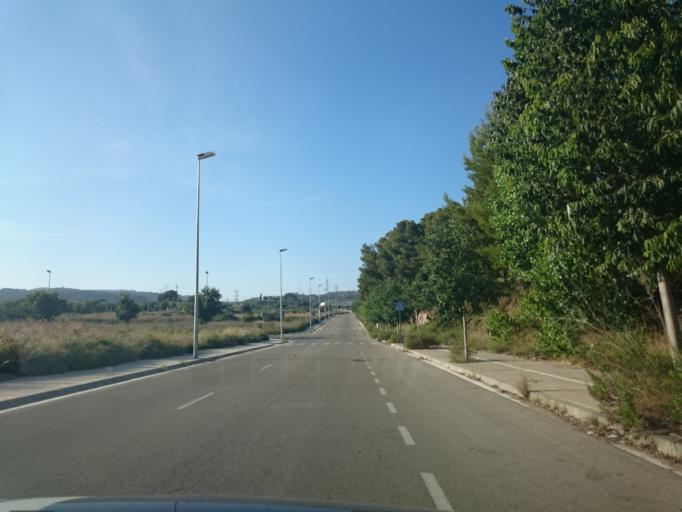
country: ES
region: Catalonia
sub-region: Provincia de Barcelona
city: Vilanova i la Geltru
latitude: 41.2464
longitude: 1.7223
